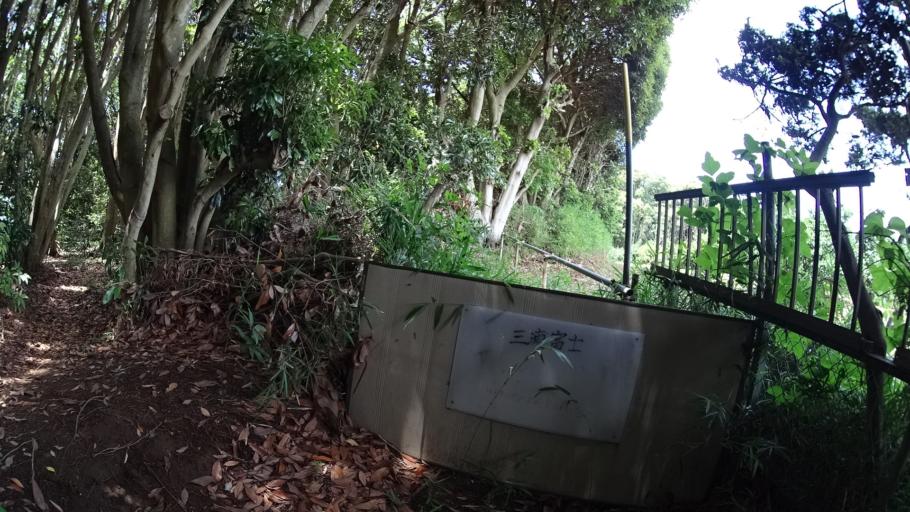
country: JP
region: Kanagawa
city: Yokosuka
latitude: 35.2089
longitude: 139.6703
